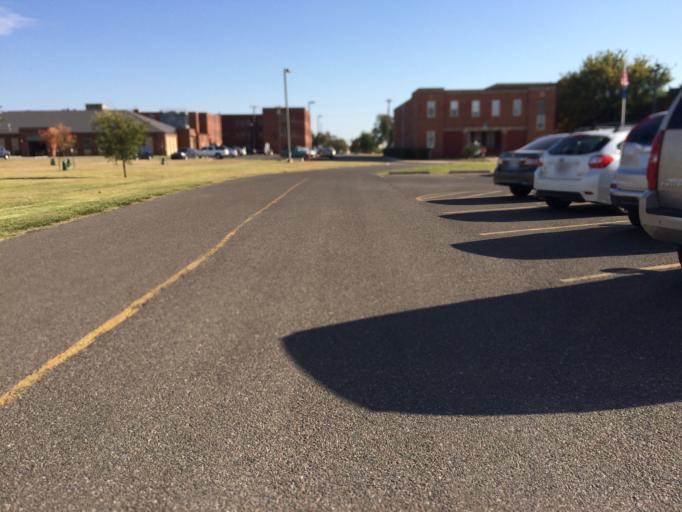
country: US
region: Oklahoma
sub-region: Cleveland County
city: Norman
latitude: 35.2299
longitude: -97.4277
